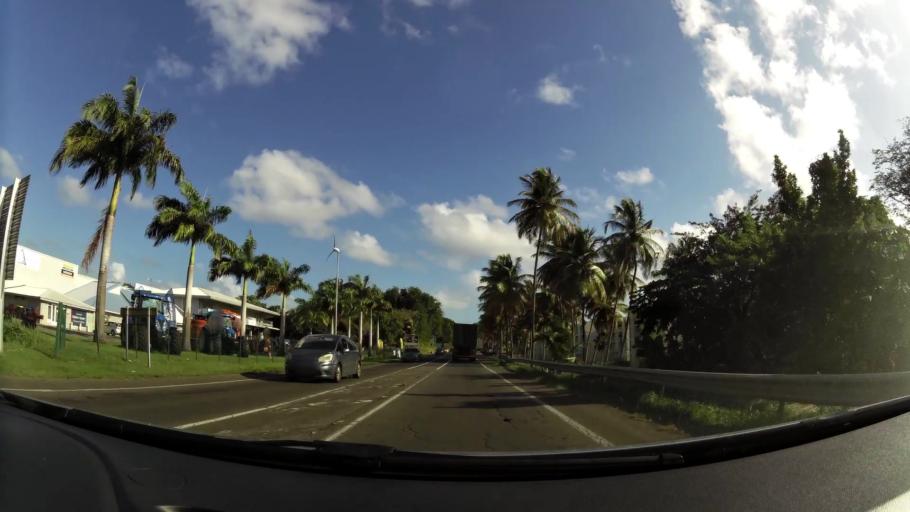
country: MQ
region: Martinique
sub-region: Martinique
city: Le Robert
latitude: 14.6759
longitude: -60.9457
